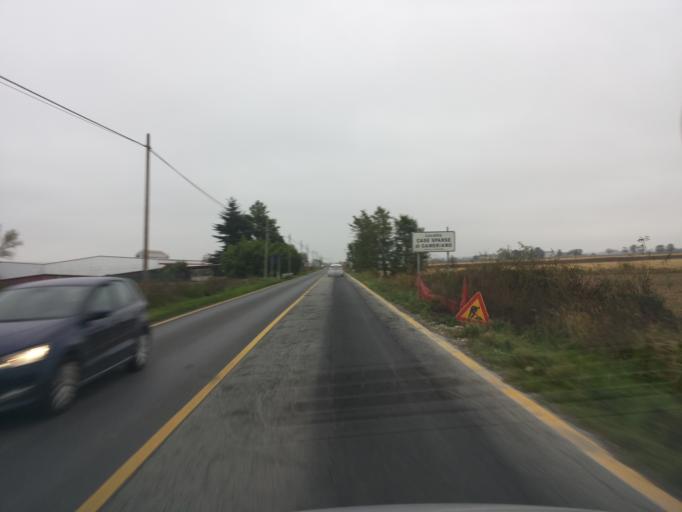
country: IT
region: Piedmont
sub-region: Provincia di Novara
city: Lumellogno
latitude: 45.4028
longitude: 8.5491
